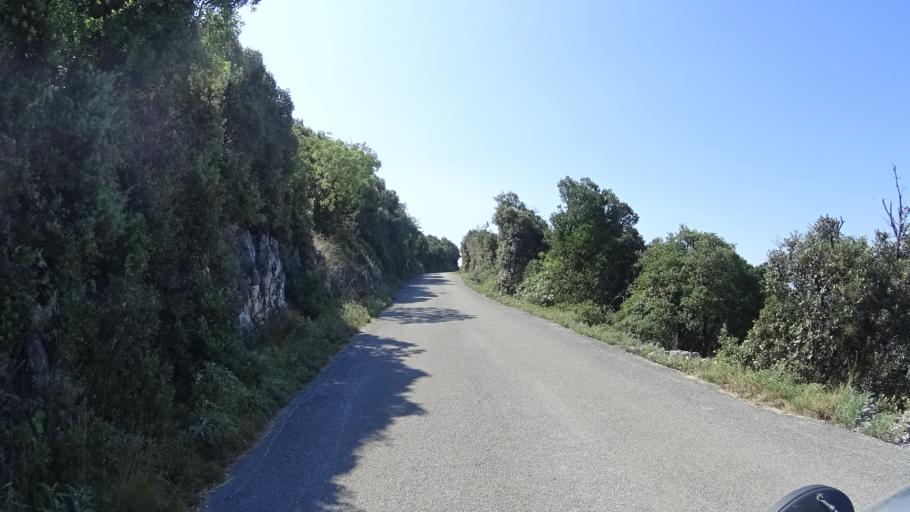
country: HR
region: Istarska
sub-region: Grad Labin
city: Rabac
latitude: 44.9705
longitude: 14.1441
